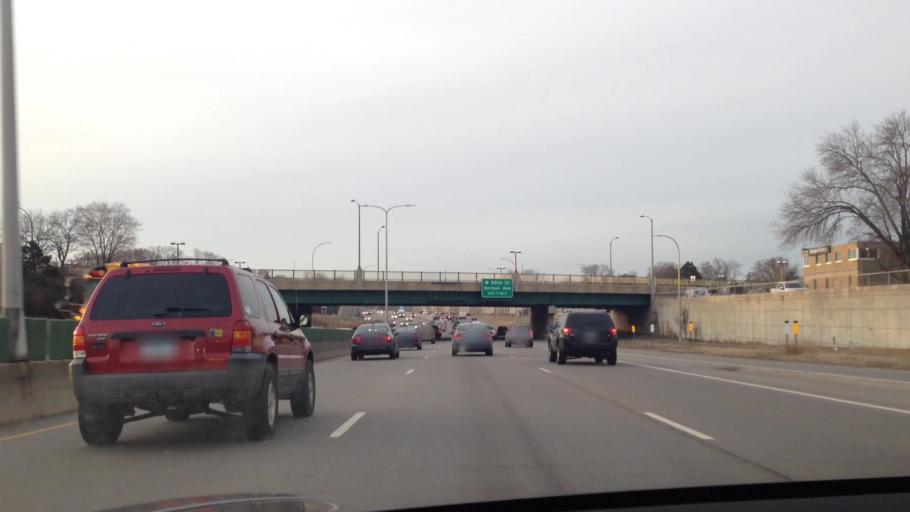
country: US
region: Minnesota
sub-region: Hennepin County
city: Saint Louis Park
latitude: 44.9315
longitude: -93.3501
